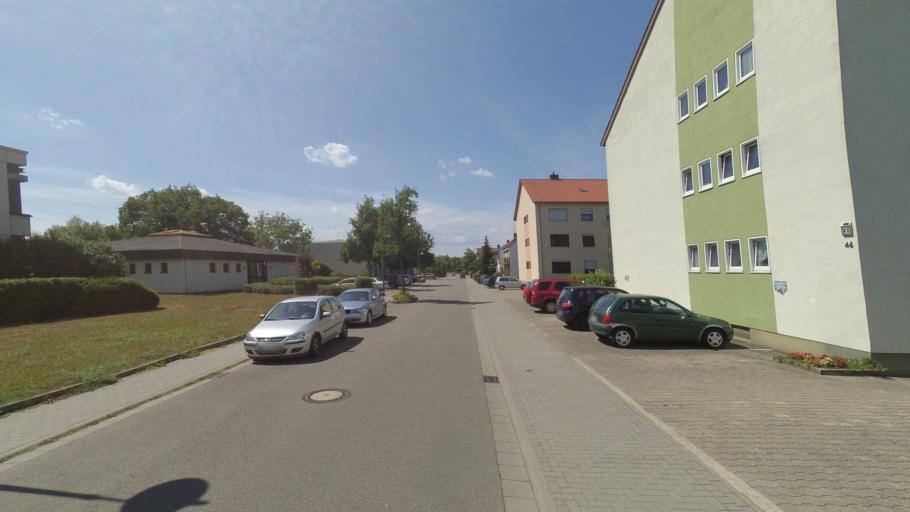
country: DE
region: Rheinland-Pfalz
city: Altrip
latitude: 49.4350
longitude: 8.4957
